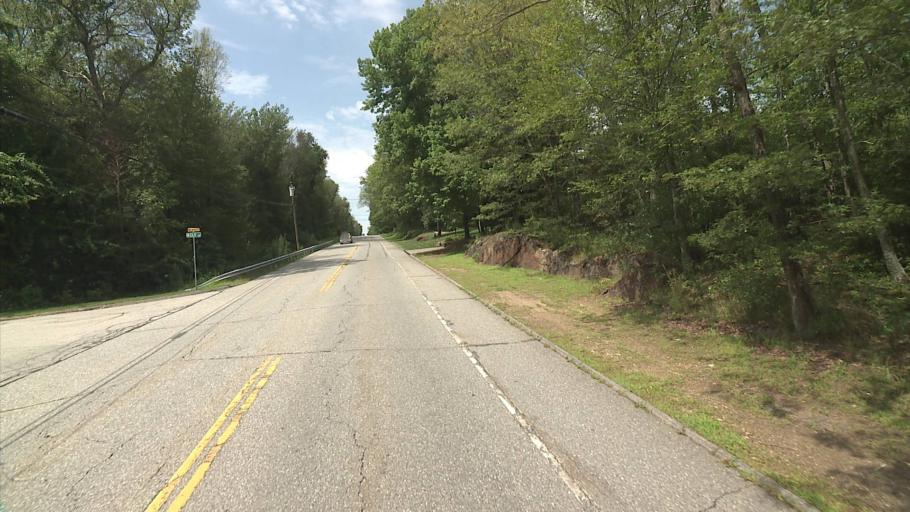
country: US
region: Connecticut
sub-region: New London County
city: Colchester
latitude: 41.5413
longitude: -72.2726
